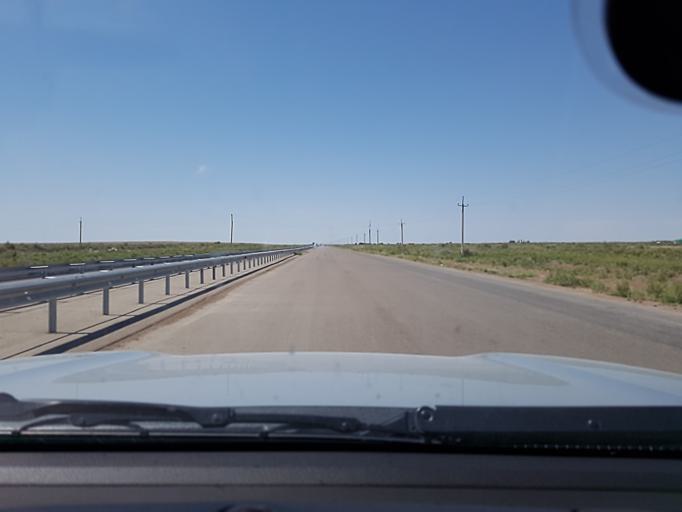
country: TM
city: Akdepe
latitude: 41.7403
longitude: 59.2137
